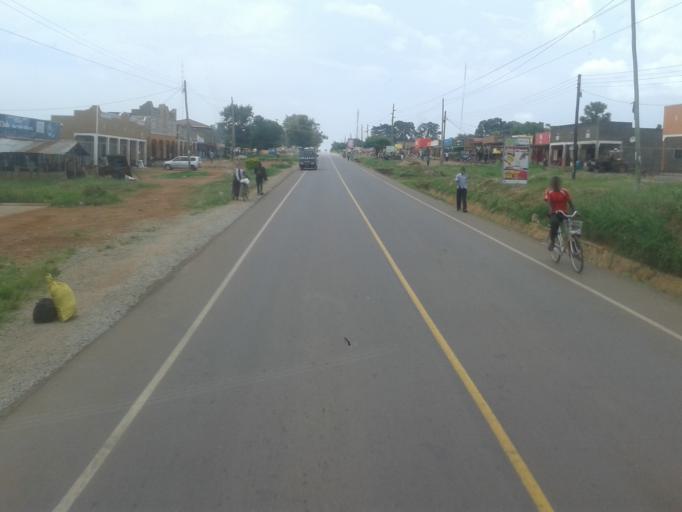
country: UG
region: Western Region
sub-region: Kiryandongo District
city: Kiryandongo
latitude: 1.8717
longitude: 32.0561
